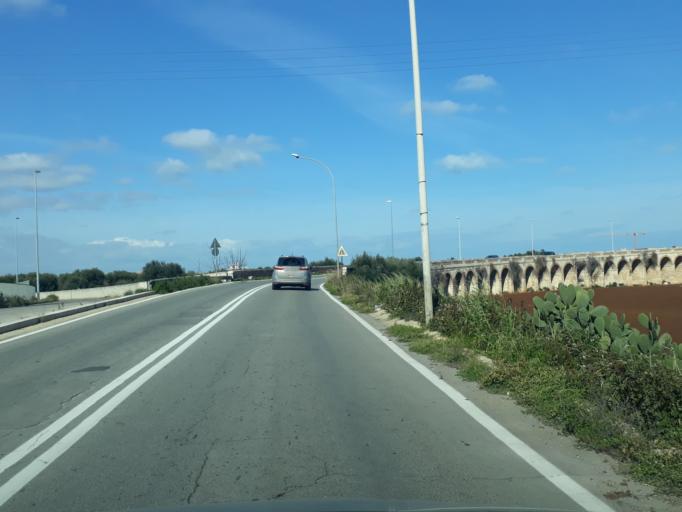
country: IT
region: Apulia
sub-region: Provincia di Bari
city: Monopoli
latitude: 40.9547
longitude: 17.2829
